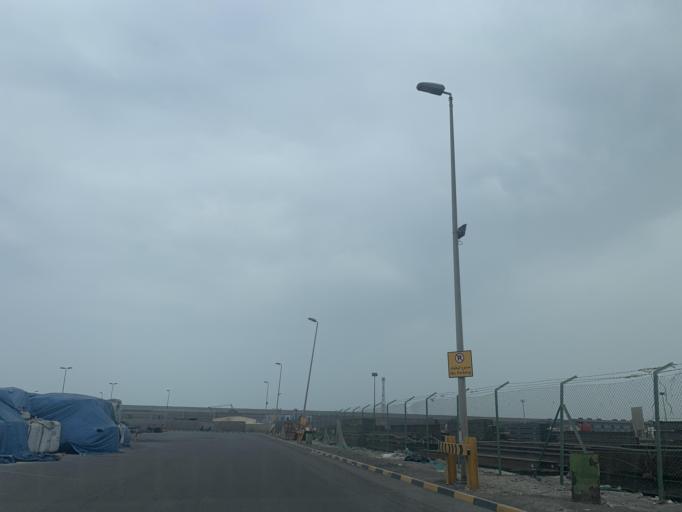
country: BH
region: Muharraq
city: Al Hadd
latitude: 26.2030
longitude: 50.6736
